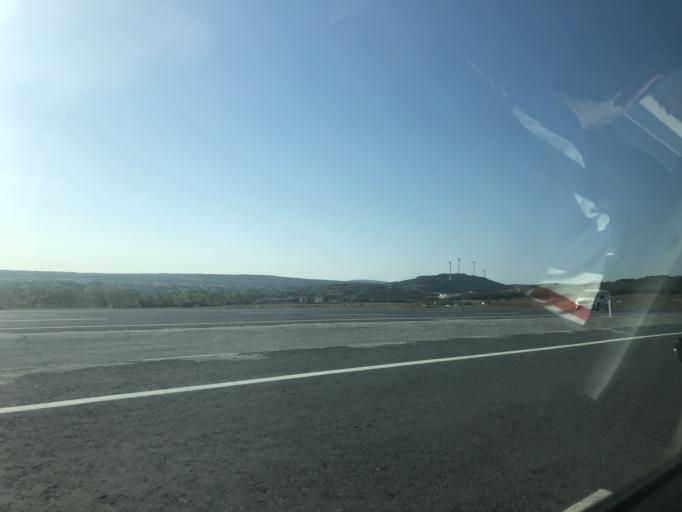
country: TR
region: Istanbul
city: Catalca
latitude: 41.1906
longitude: 28.4634
